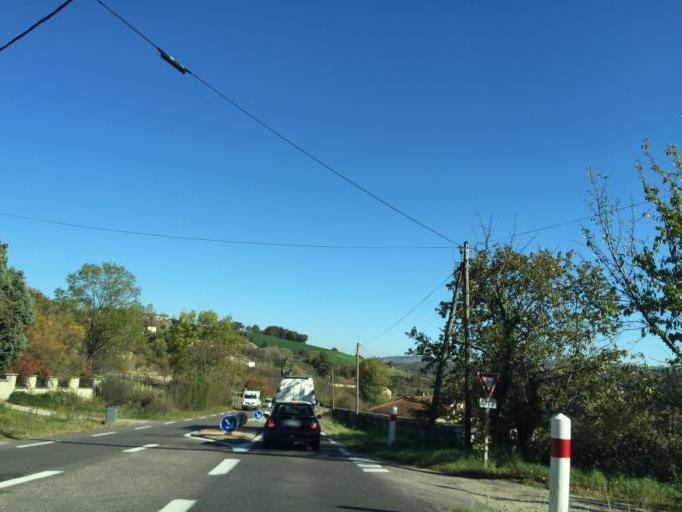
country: FR
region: Rhone-Alpes
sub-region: Departement de la Loire
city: Chateauneuf
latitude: 45.5455
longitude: 4.6433
